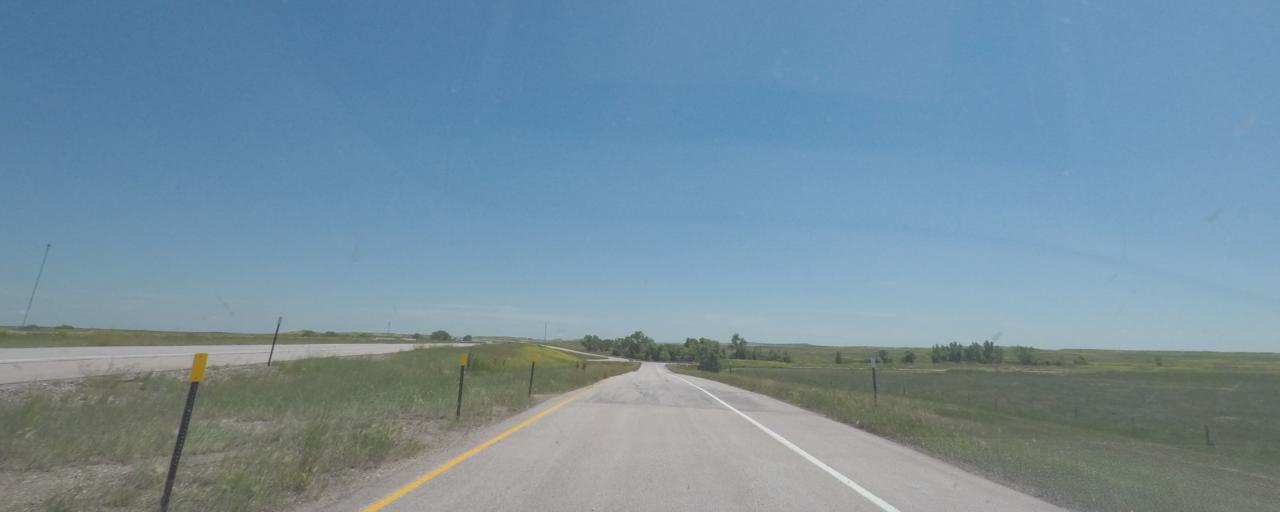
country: US
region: South Dakota
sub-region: Haakon County
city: Philip
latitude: 43.9388
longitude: -102.1546
